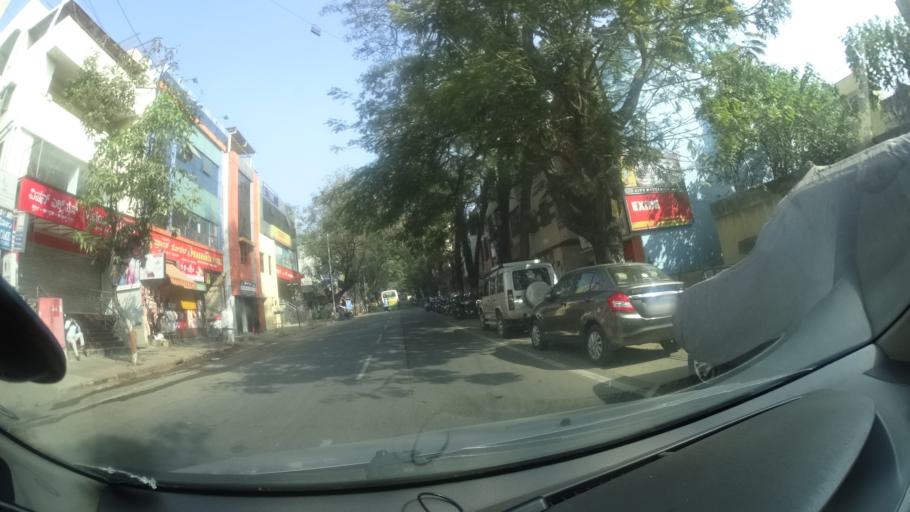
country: IN
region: Karnataka
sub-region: Bangalore Urban
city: Bangalore
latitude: 13.0072
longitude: 77.5712
